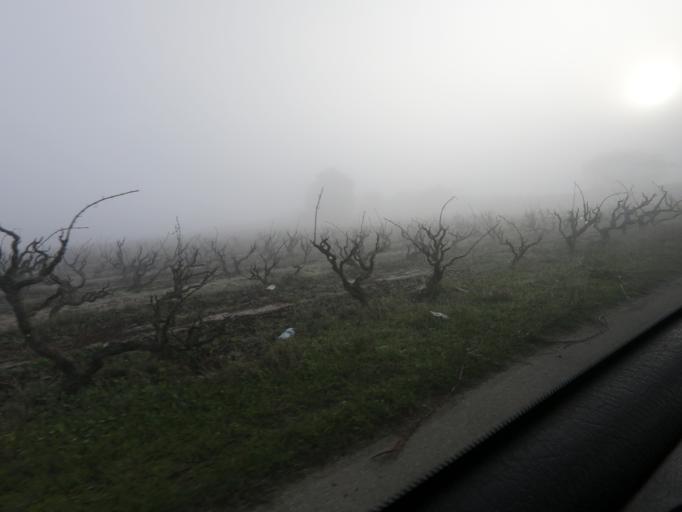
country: PT
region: Setubal
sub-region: Palmela
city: Palmela
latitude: 38.5994
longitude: -8.8458
